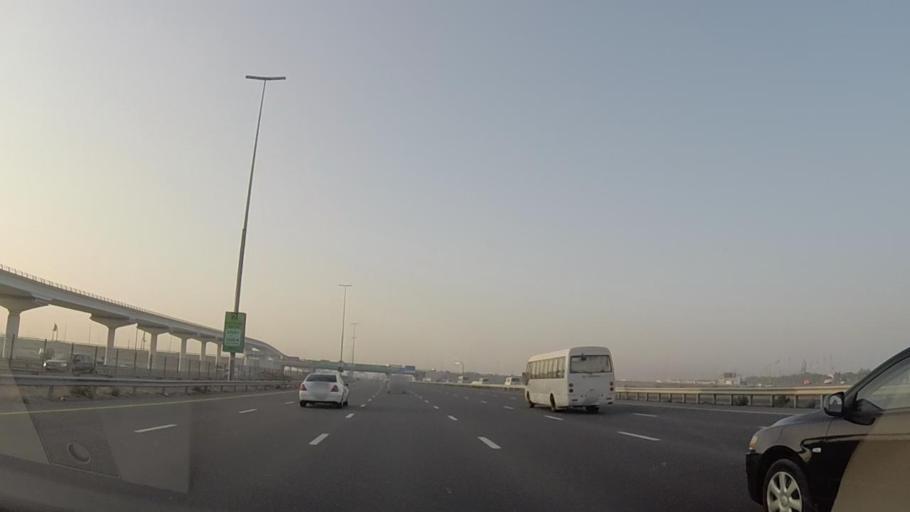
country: AE
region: Dubai
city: Dubai
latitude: 25.0205
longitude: 55.0984
